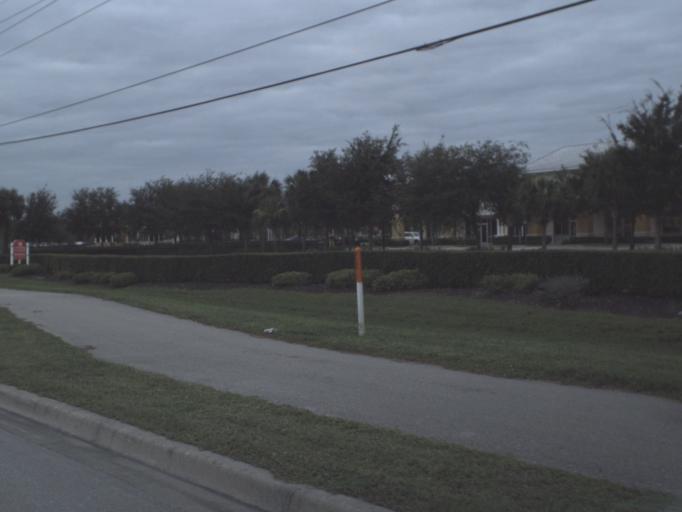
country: US
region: Florida
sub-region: Collier County
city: Golden Gate
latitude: 26.1522
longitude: -81.6867
